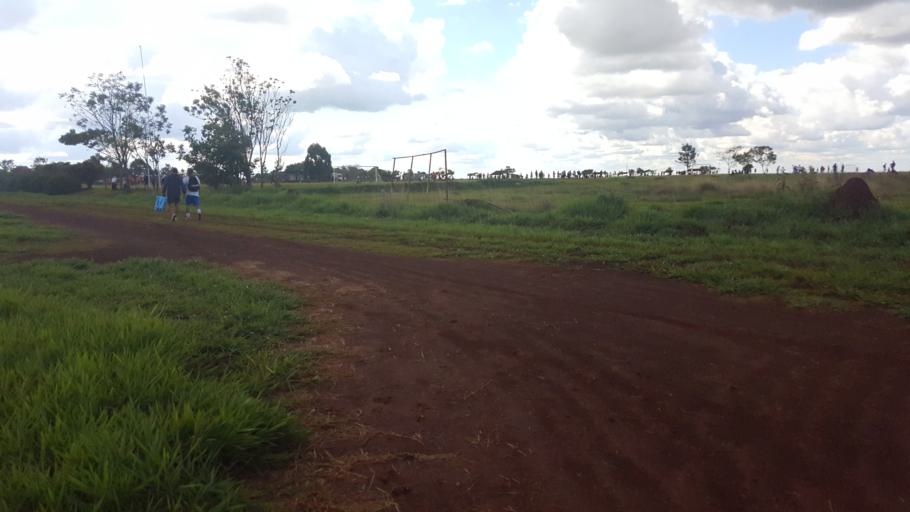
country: AR
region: Misiones
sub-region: Departamento de Capital
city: Posadas
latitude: -27.4169
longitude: -56.0072
